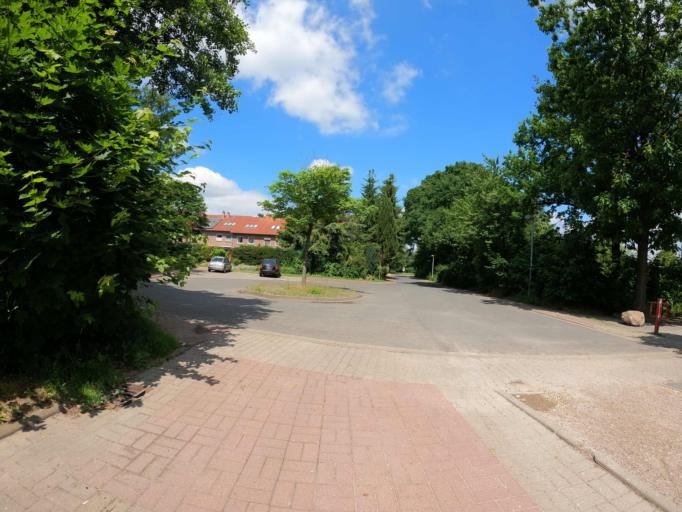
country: DE
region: Schleswig-Holstein
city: Wentorf bei Hamburg
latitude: 53.4963
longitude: 10.2563
